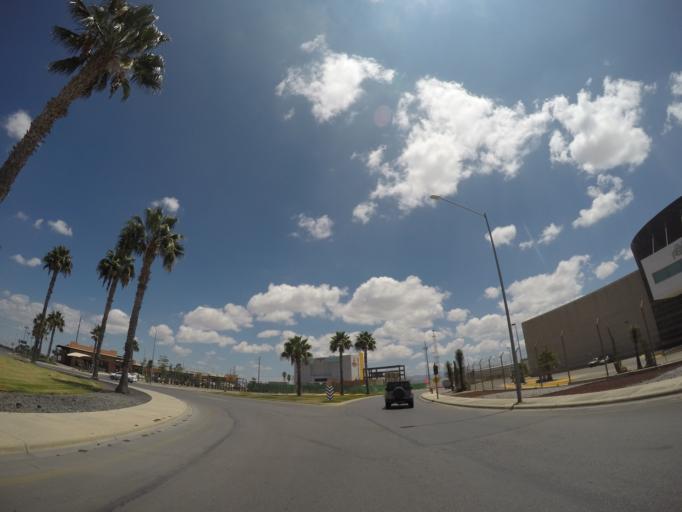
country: MX
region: San Luis Potosi
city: La Pila
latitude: 22.0403
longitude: -100.8939
